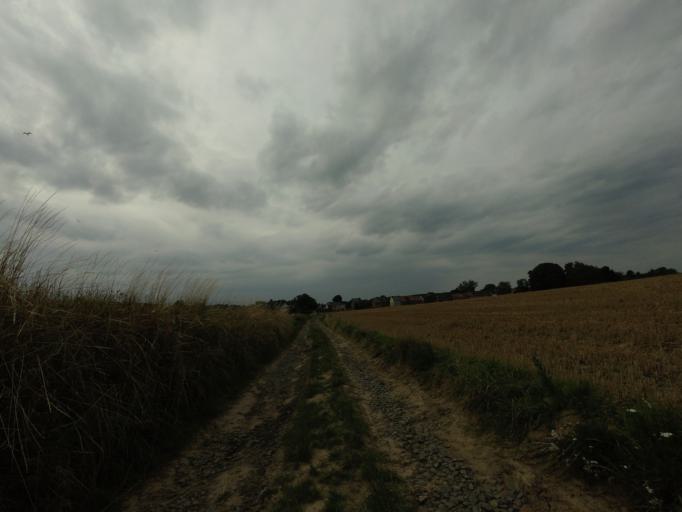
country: BE
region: Flanders
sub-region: Provincie Vlaams-Brabant
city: Grimbergen
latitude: 50.9265
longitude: 4.3822
